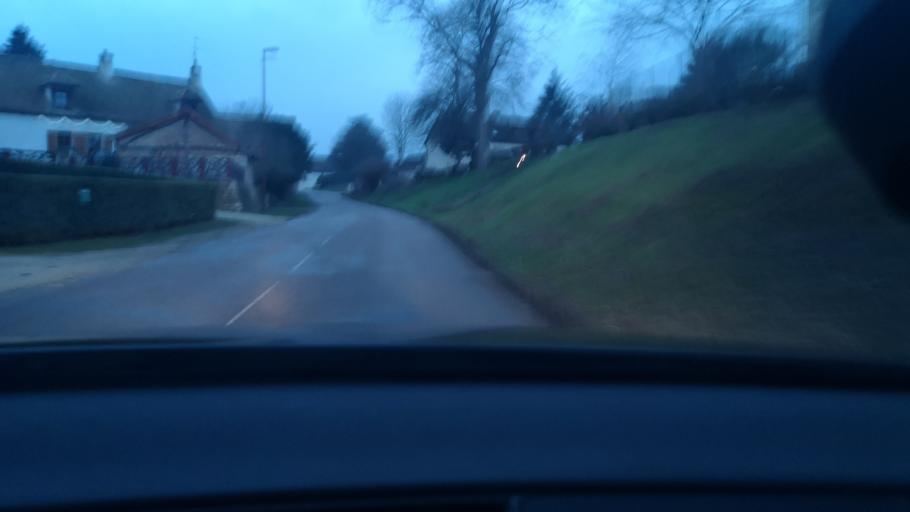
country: FR
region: Bourgogne
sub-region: Departement de Saone-et-Loire
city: Gergy
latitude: 46.9576
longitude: 4.9214
